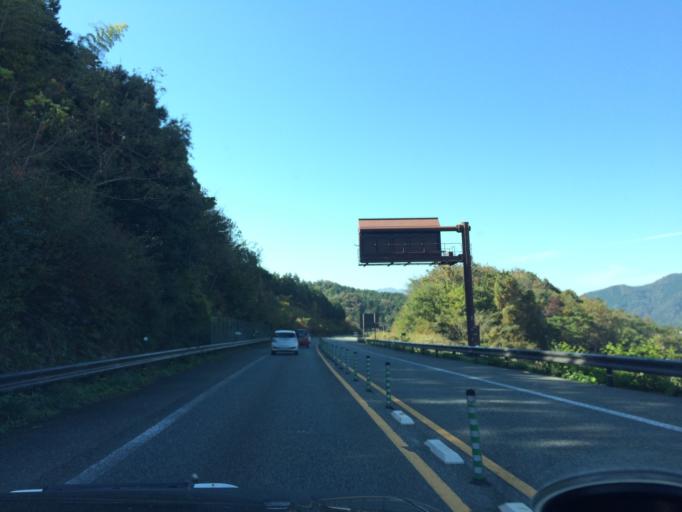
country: JP
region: Kyoto
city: Fukuchiyama
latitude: 35.3027
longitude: 134.9003
